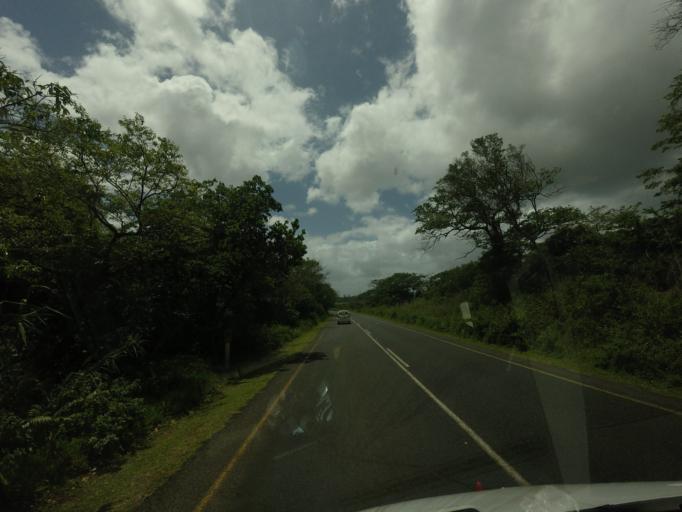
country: ZA
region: KwaZulu-Natal
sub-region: uMkhanyakude District Municipality
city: Mtubatuba
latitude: -28.3737
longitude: 32.3951
